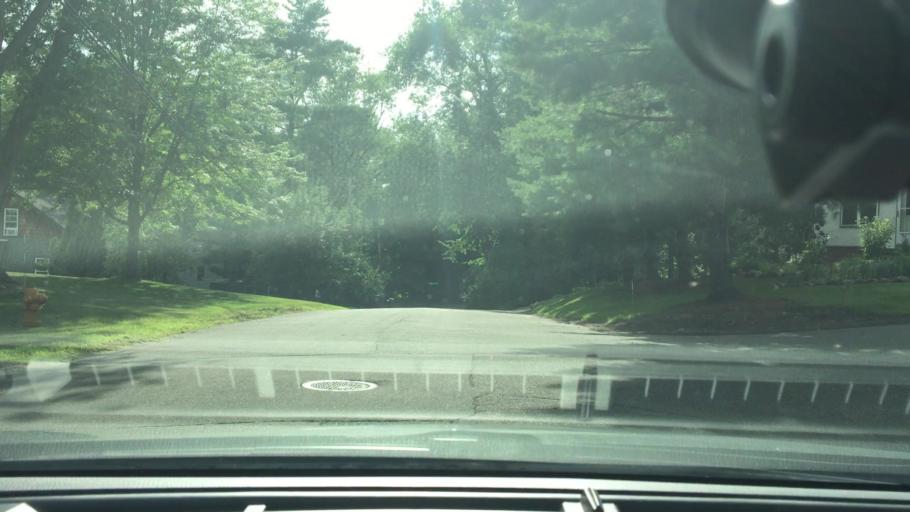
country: US
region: Minnesota
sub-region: Hennepin County
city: Plymouth
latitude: 45.0038
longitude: -93.4321
